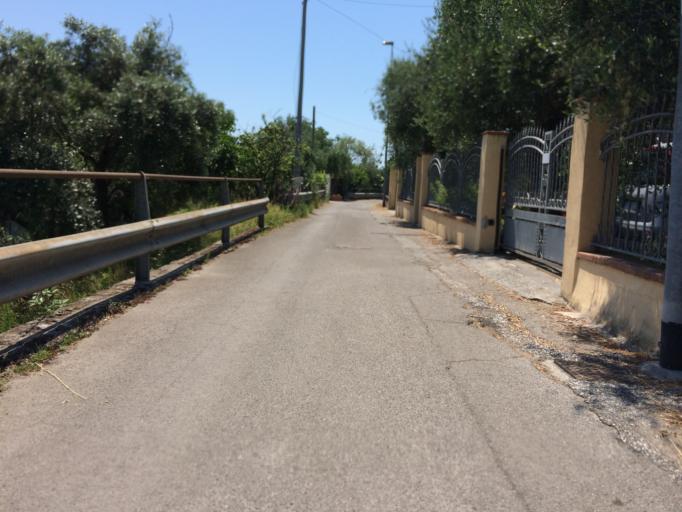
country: IT
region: Tuscany
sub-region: Provincia di Massa-Carrara
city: Massa
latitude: 44.0371
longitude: 10.1302
